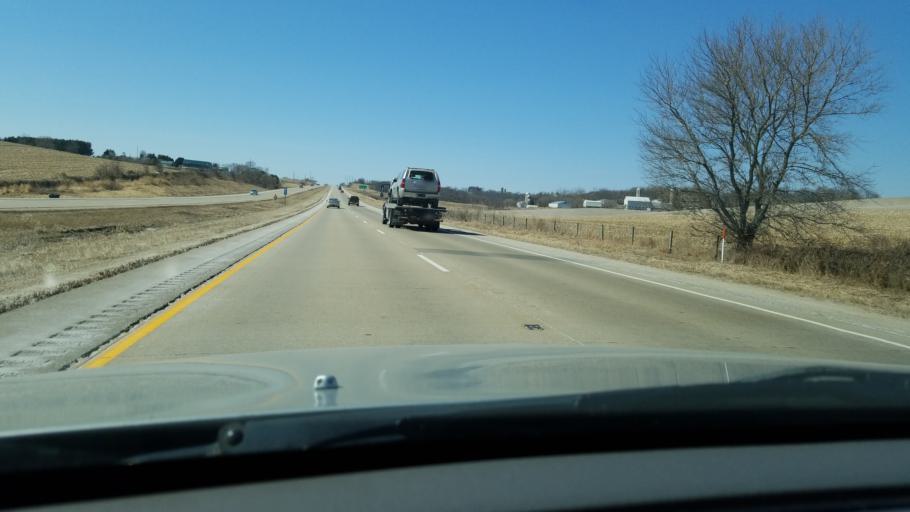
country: US
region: Wisconsin
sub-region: Dane County
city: Verona
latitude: 42.9878
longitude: -89.5924
